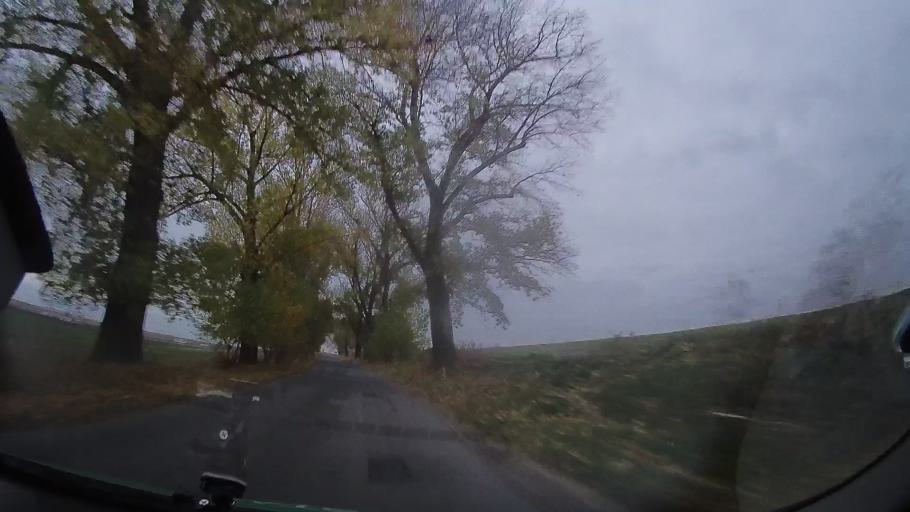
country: RO
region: Tulcea
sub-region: Comuna Mihai Bravu
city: Turda
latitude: 44.9669
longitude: 28.6316
